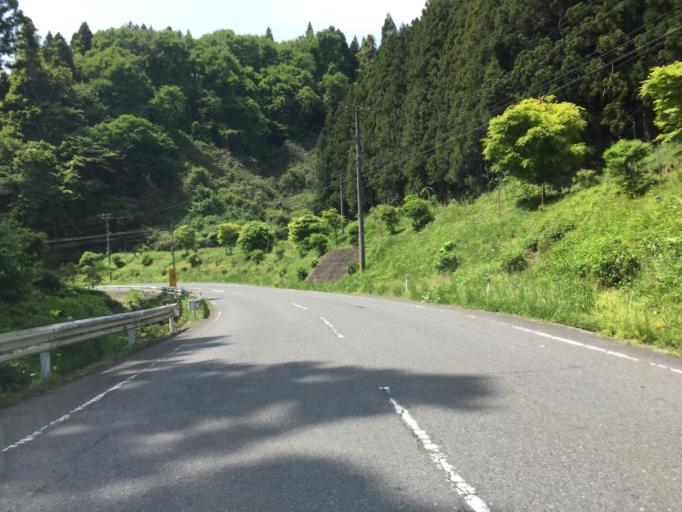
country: JP
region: Fukushima
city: Ishikawa
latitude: 37.1526
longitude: 140.4878
